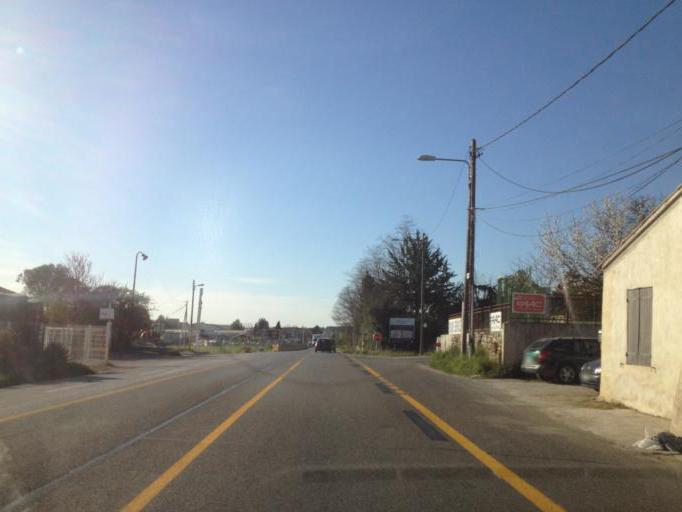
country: FR
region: Provence-Alpes-Cote d'Azur
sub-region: Departement des Bouches-du-Rhone
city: Eguilles
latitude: 43.5774
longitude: 5.3841
